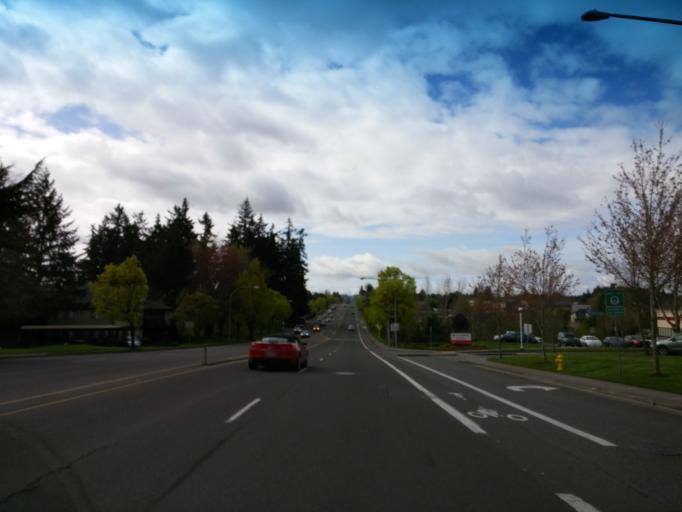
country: US
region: Oregon
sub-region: Washington County
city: Rockcreek
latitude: 45.5336
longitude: -122.8676
